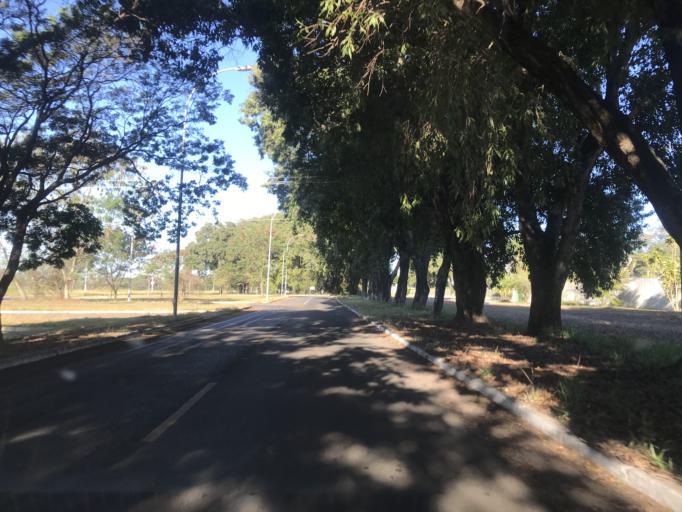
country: BR
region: Federal District
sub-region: Brasilia
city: Brasilia
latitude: -15.8241
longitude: -47.8913
